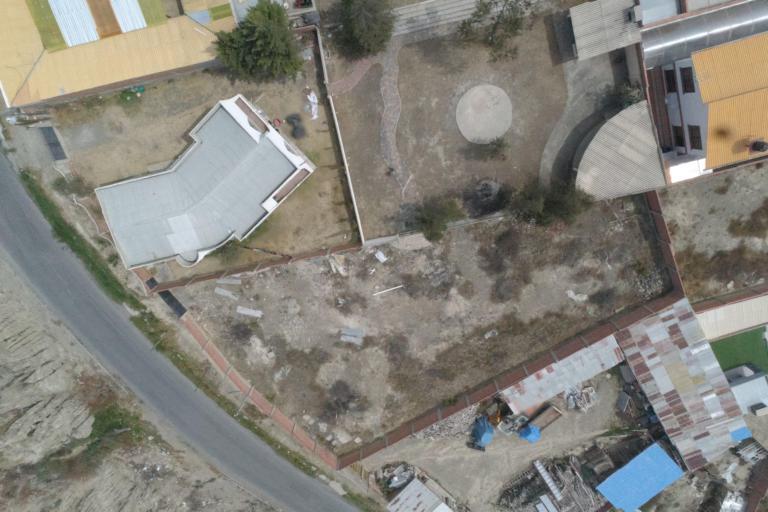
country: BO
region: La Paz
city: La Paz
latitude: -16.6013
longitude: -68.0699
